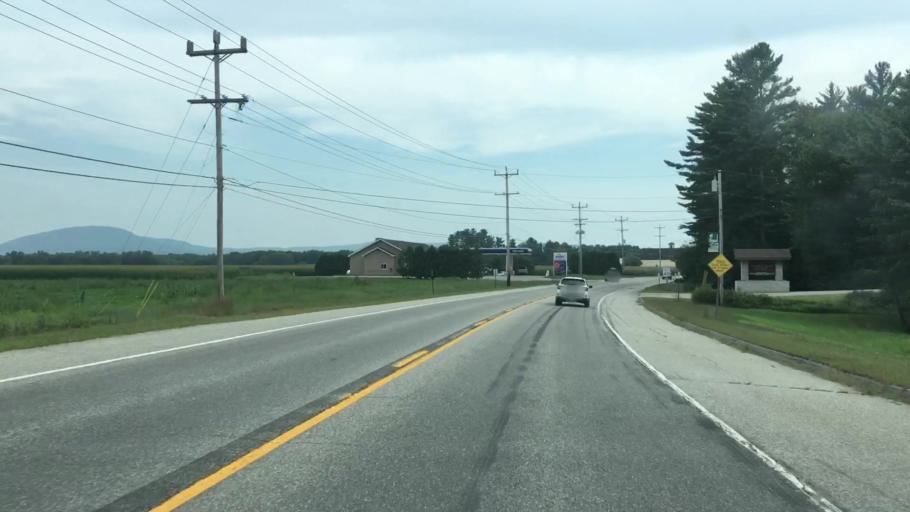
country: US
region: Maine
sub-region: Oxford County
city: Bethel
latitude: 44.4265
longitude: -70.7980
